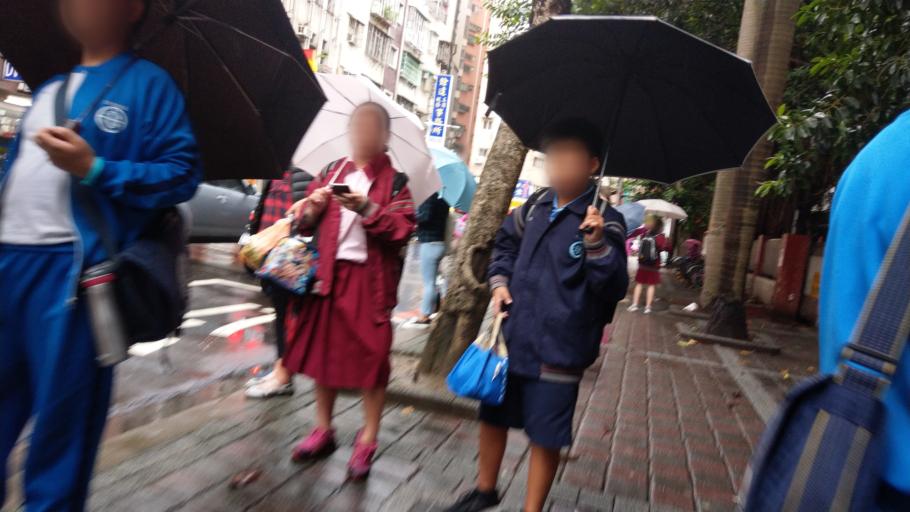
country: TW
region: Taipei
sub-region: Taipei
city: Banqiao
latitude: 24.9978
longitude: 121.4634
